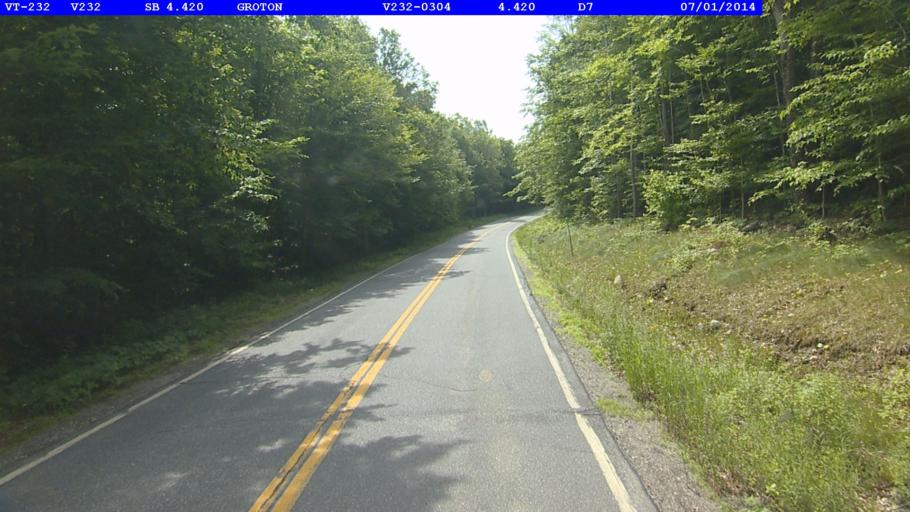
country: US
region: Vermont
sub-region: Washington County
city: Barre
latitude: 44.2663
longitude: -72.2739
